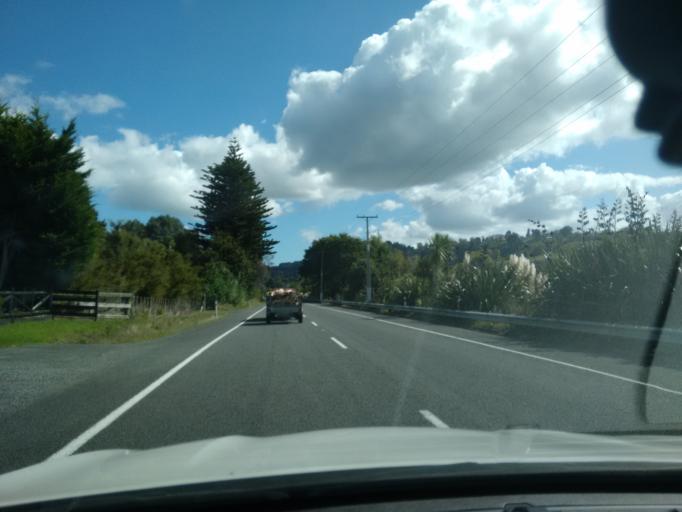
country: NZ
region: Manawatu-Wanganui
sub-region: Wanganui District
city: Wanganui
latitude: -39.8966
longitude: 175.0832
